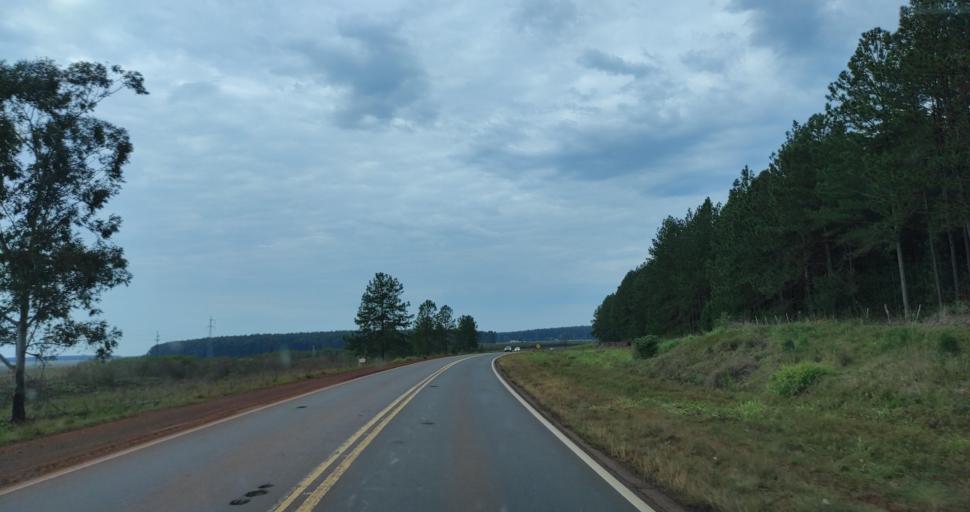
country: AR
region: Corrientes
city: Gobernador Ingeniero Valentin Virasoro
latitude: -28.2518
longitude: -56.1016
